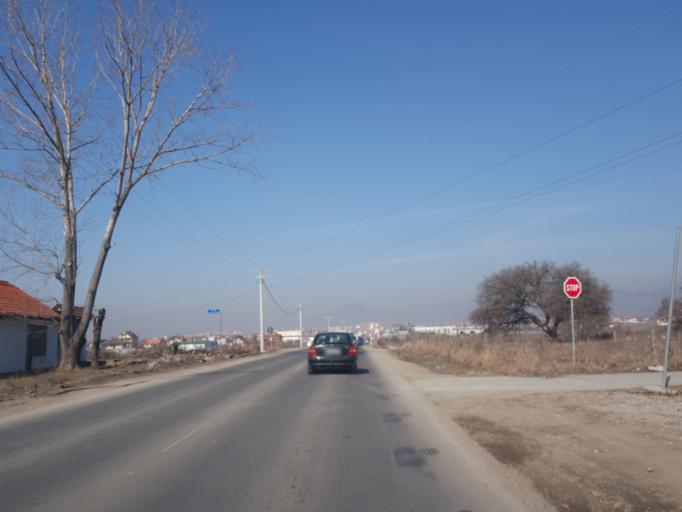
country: XK
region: Mitrovica
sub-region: Vushtrri
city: Vushtrri
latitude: 42.8022
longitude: 20.9937
